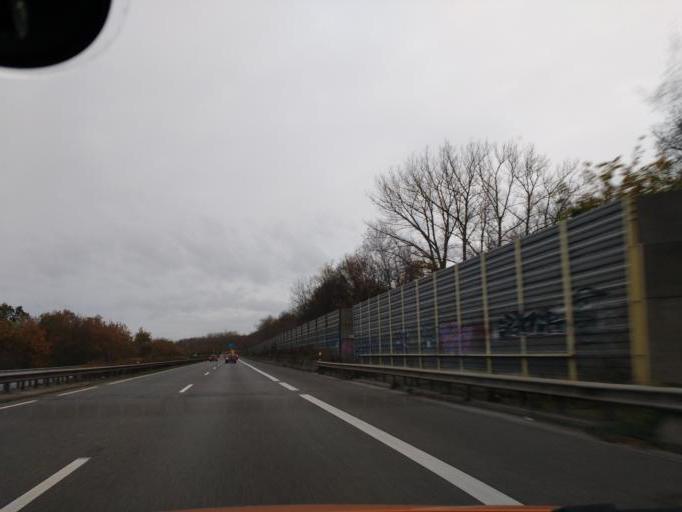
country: DE
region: Lower Saxony
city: Delmenhorst
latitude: 53.0418
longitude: 8.5828
